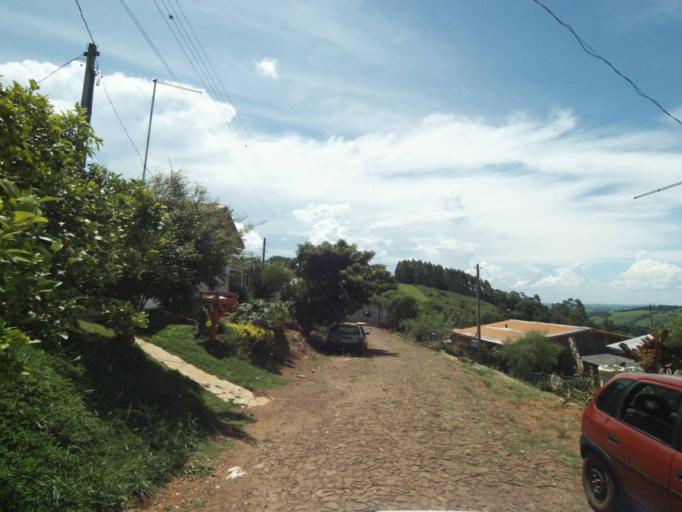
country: BR
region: Parana
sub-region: Guaraniacu
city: Guaraniacu
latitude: -25.0901
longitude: -52.8742
